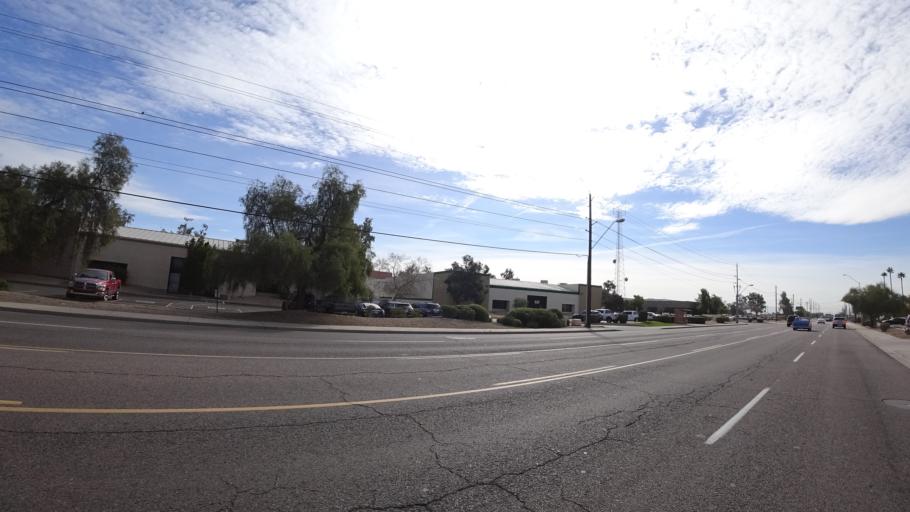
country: US
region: Arizona
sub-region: Maricopa County
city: Phoenix
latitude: 33.4487
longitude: -112.1519
